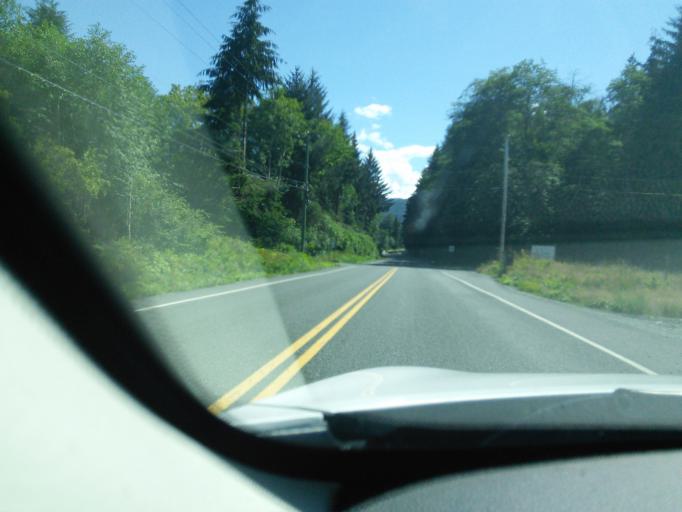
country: CA
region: British Columbia
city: Campbell River
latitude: 50.3257
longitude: -125.9221
